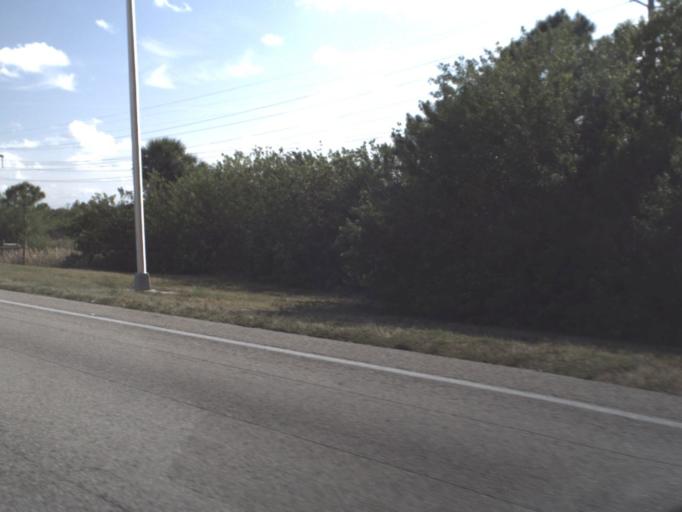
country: US
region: Florida
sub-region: Brevard County
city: June Park
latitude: 28.1247
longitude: -80.7061
